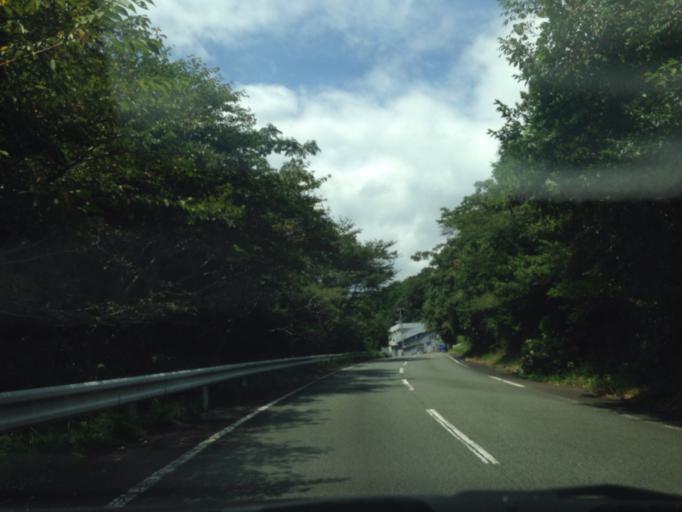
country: JP
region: Shizuoka
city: Shimoda
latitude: 34.6306
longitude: 138.8217
